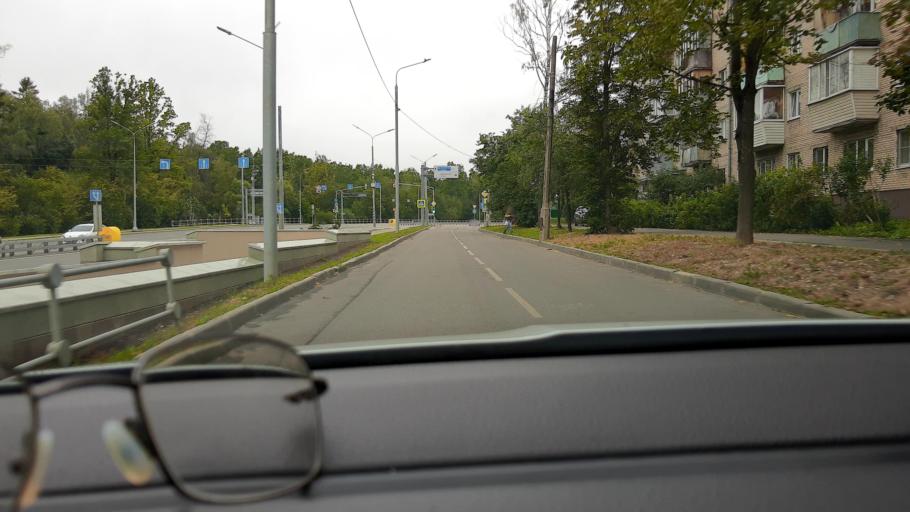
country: RU
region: Moskovskaya
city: Kokoshkino
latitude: 55.5993
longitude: 37.1597
